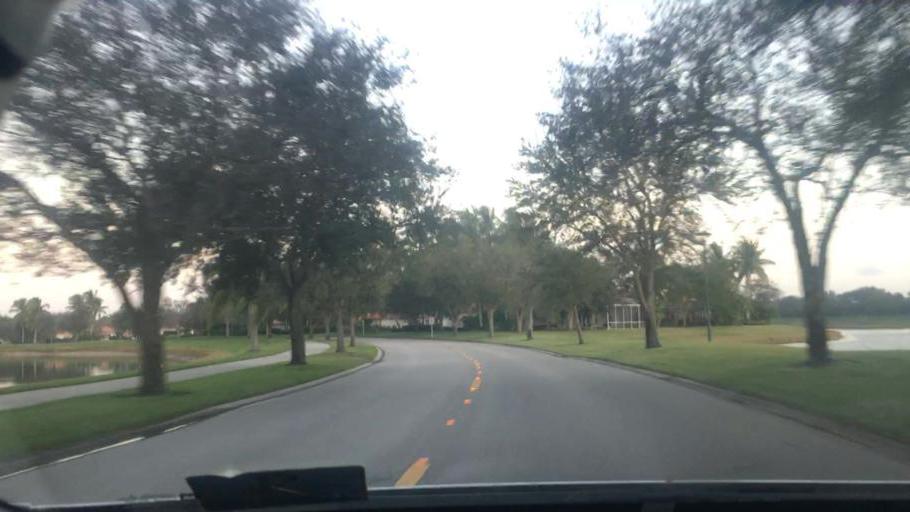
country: US
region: Florida
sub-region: Palm Beach County
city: Plantation Mobile Home Park
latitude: 26.7106
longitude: -80.1653
